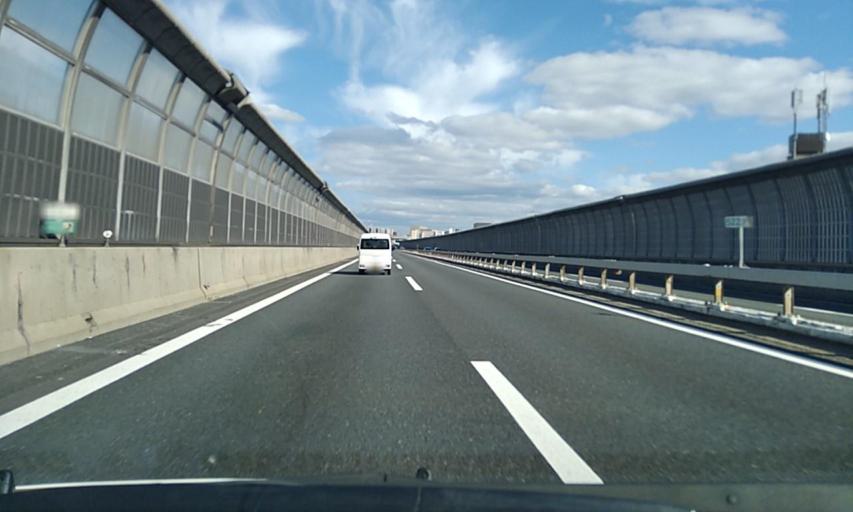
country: JP
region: Osaka
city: Toyonaka
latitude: 34.7592
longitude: 135.4833
